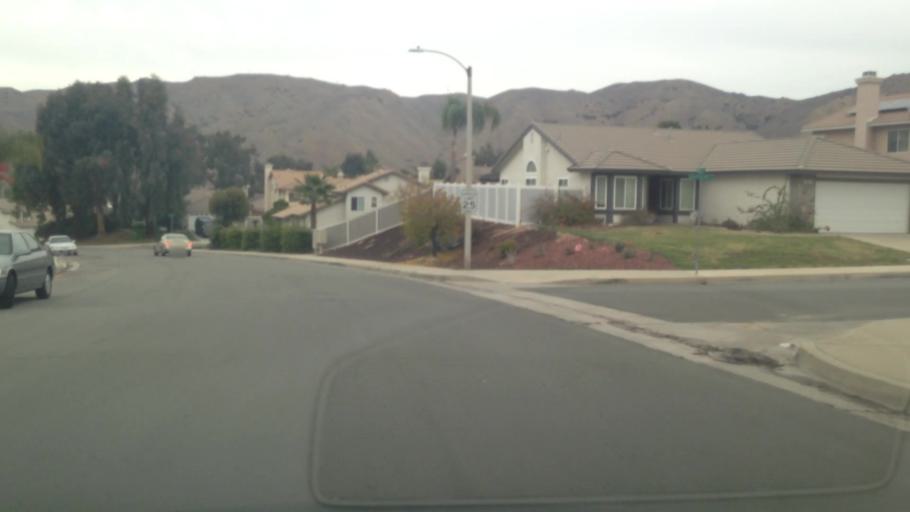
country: US
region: California
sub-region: Riverside County
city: Lake Elsinore
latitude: 33.7320
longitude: -117.4304
